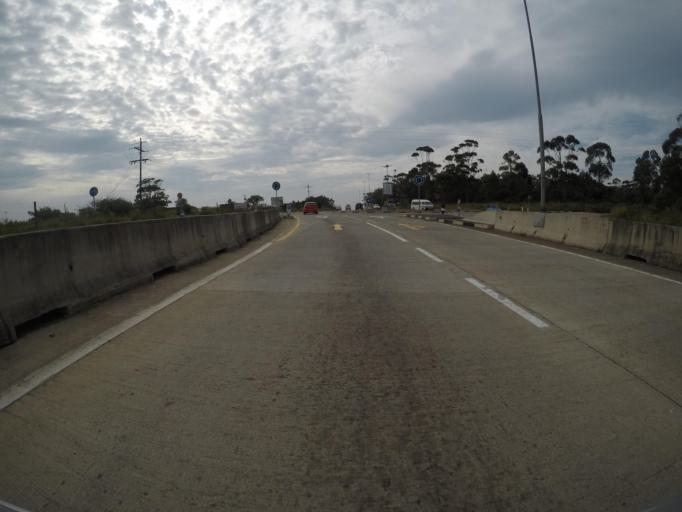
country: ZA
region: Eastern Cape
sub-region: Buffalo City Metropolitan Municipality
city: East London
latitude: -32.9402
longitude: 27.9604
